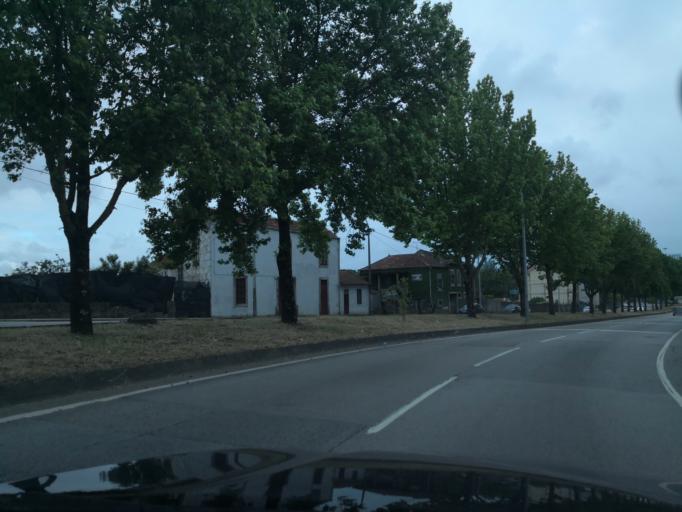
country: PT
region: Porto
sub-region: Gondomar
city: Rio Tinto
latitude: 41.1714
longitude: -8.5674
